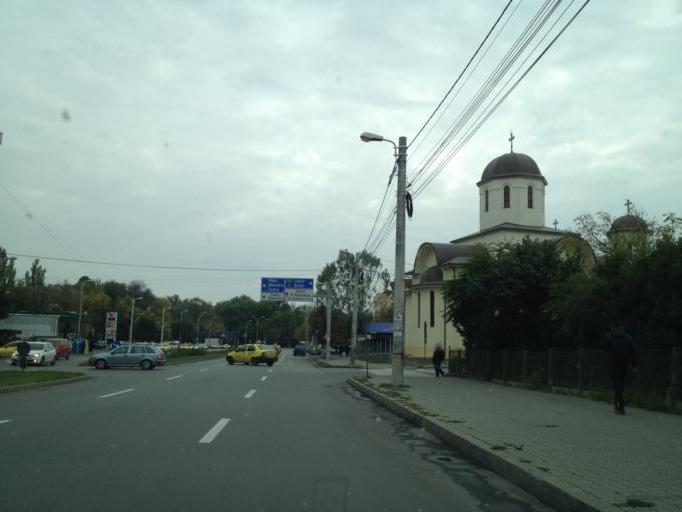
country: RO
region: Dolj
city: Craiova
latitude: 44.3020
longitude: 23.7973
